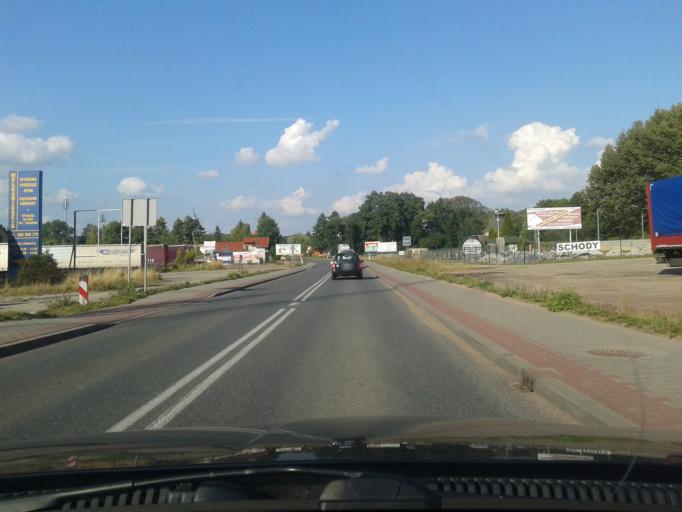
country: PL
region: Silesian Voivodeship
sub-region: Powiat wodzislawski
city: Wodzislaw Slaski
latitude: 49.9930
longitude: 18.4562
